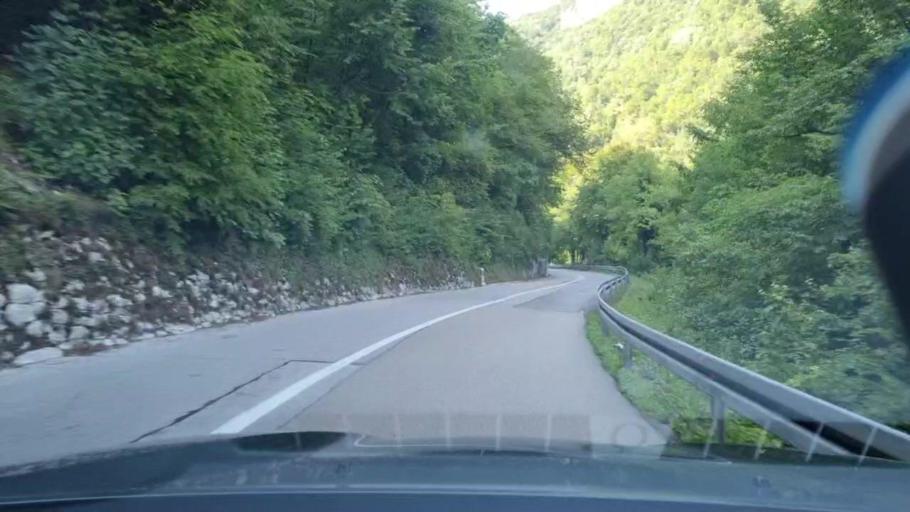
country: BA
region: Federation of Bosnia and Herzegovina
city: Stijena
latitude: 44.8791
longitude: 16.0706
